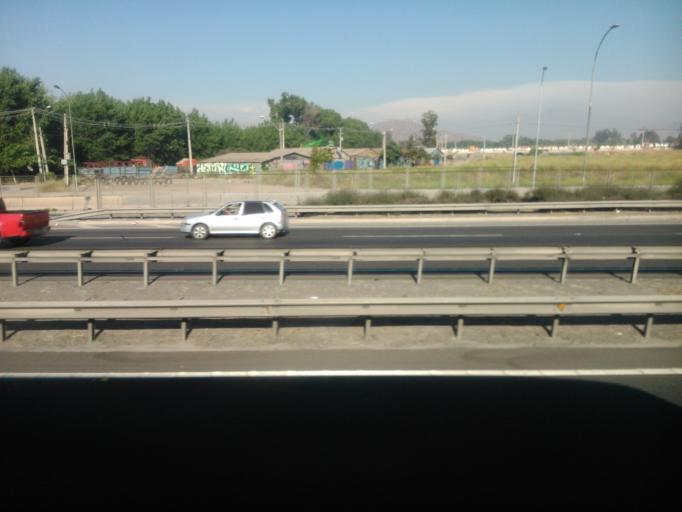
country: CL
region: Santiago Metropolitan
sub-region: Provincia de Maipo
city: San Bernardo
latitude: -33.6258
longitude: -70.7143
